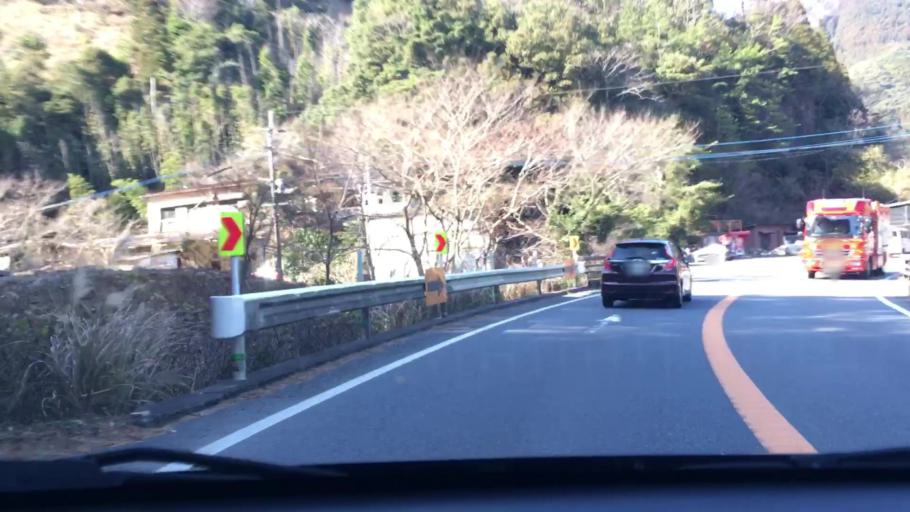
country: JP
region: Oita
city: Tsukumiura
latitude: 32.9975
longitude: 131.8159
